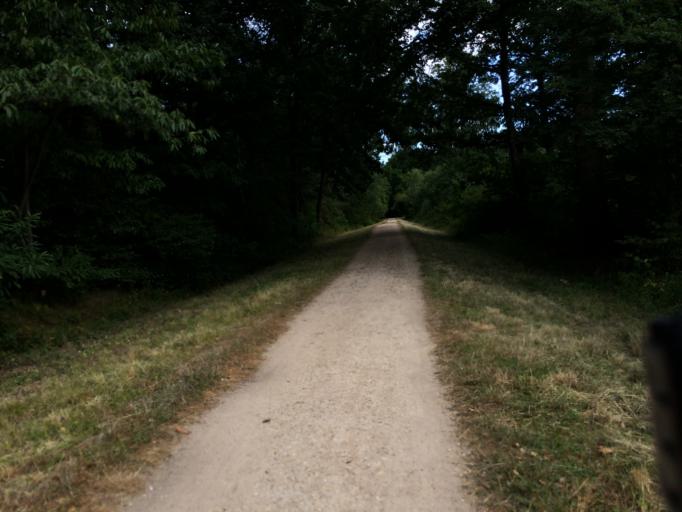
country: FR
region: Ile-de-France
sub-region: Departement de l'Essonne
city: Soisy-sur-Seine
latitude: 48.6709
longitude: 2.4477
